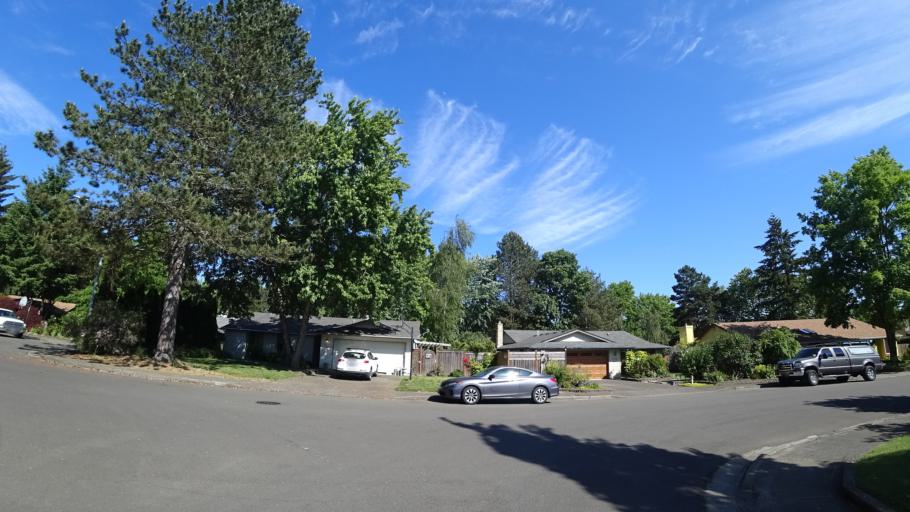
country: US
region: Oregon
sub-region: Washington County
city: Beaverton
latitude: 45.4555
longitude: -122.8028
